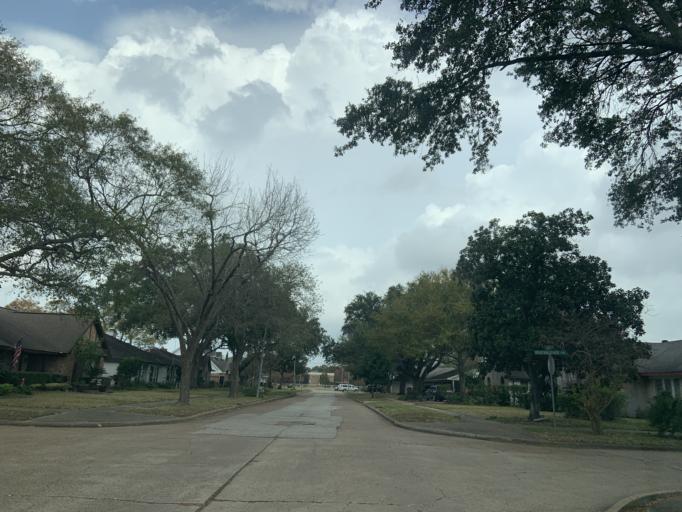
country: US
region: Texas
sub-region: Harris County
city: Bellaire
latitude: 29.6758
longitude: -95.4999
